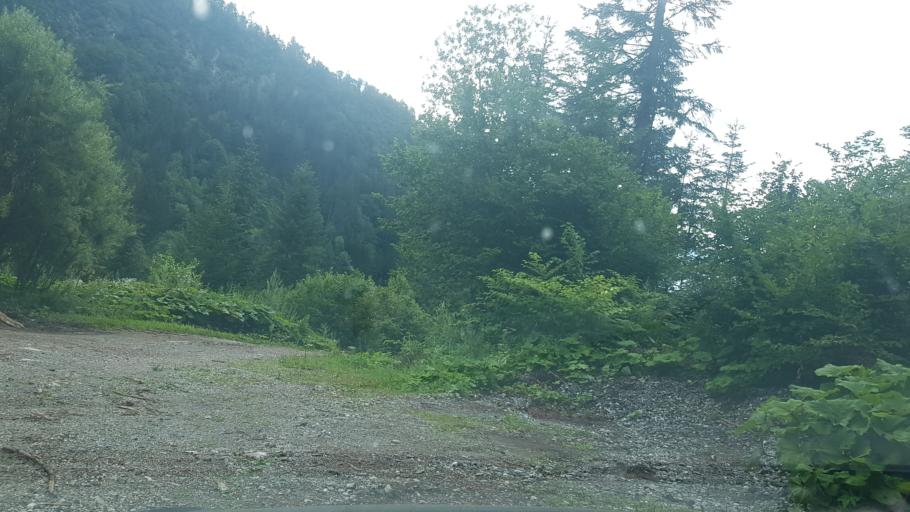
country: IT
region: Friuli Venezia Giulia
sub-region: Provincia di Udine
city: Forni Avoltri
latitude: 46.5777
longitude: 12.7876
